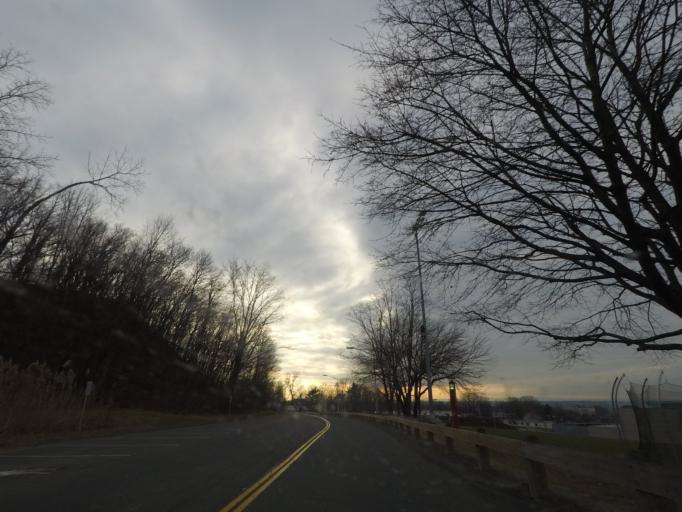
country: US
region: New York
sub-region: Rensselaer County
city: Troy
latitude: 42.7322
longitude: -73.6657
